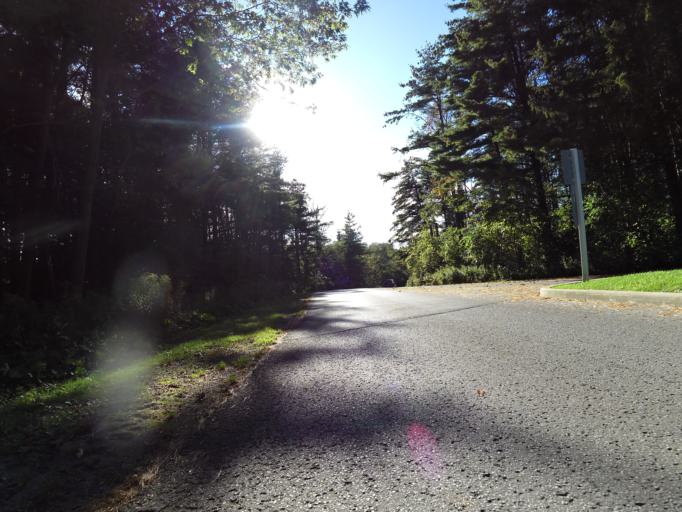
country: CA
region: Ontario
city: Oshawa
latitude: 43.8750
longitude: -78.7798
